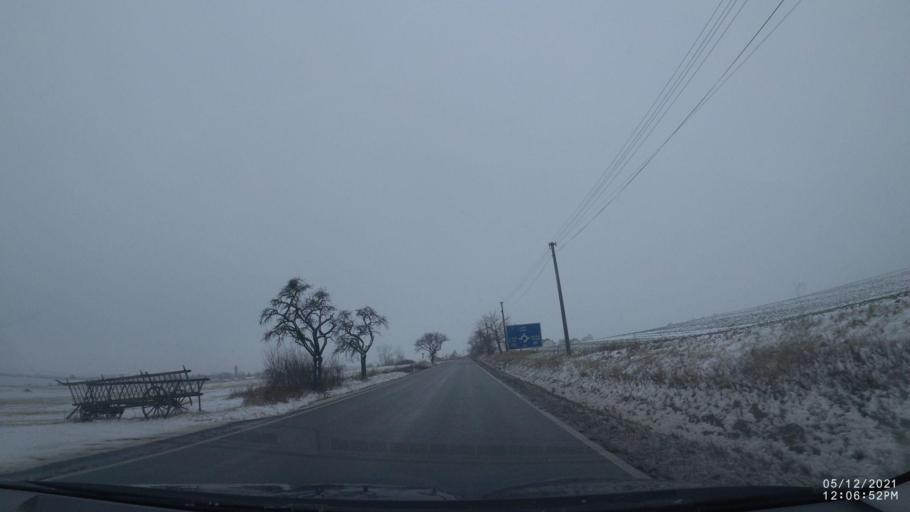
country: CZ
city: Ceske Mezirici
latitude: 50.2958
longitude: 16.0182
